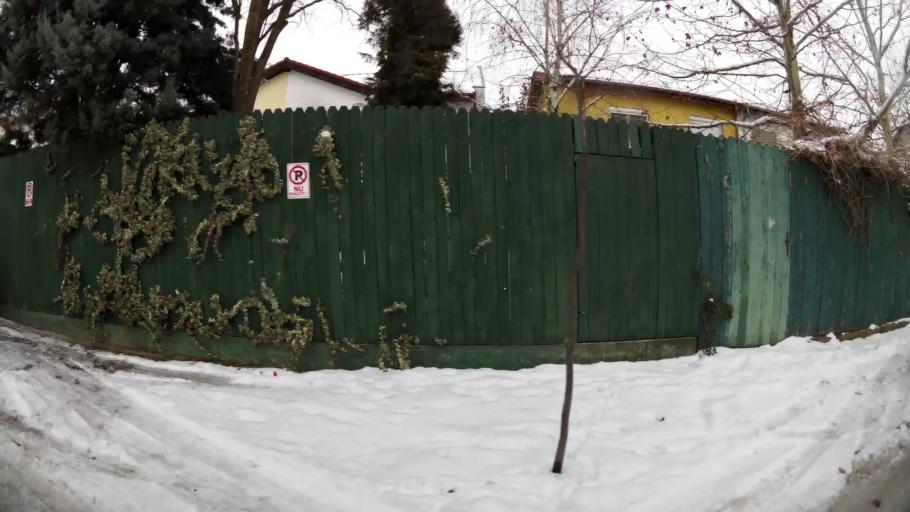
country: RO
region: Ilfov
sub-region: Comuna Tunari
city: Tunari
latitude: 44.5107
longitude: 26.1139
